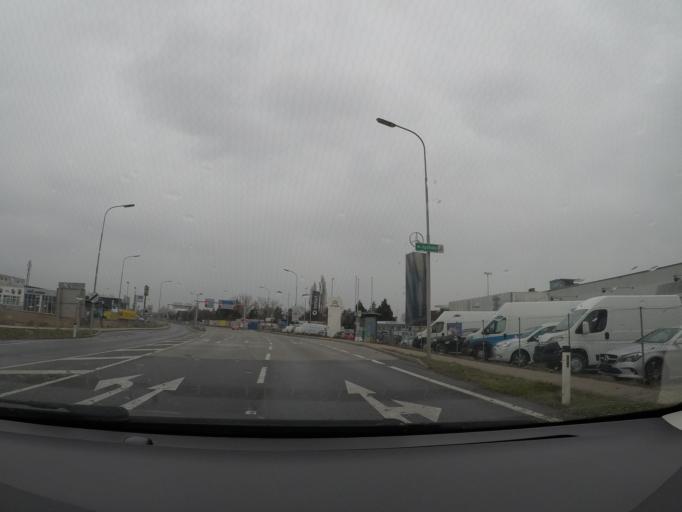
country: AT
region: Lower Austria
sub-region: Politischer Bezirk Modling
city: Brunn am Gebirge
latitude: 48.1116
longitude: 16.3050
